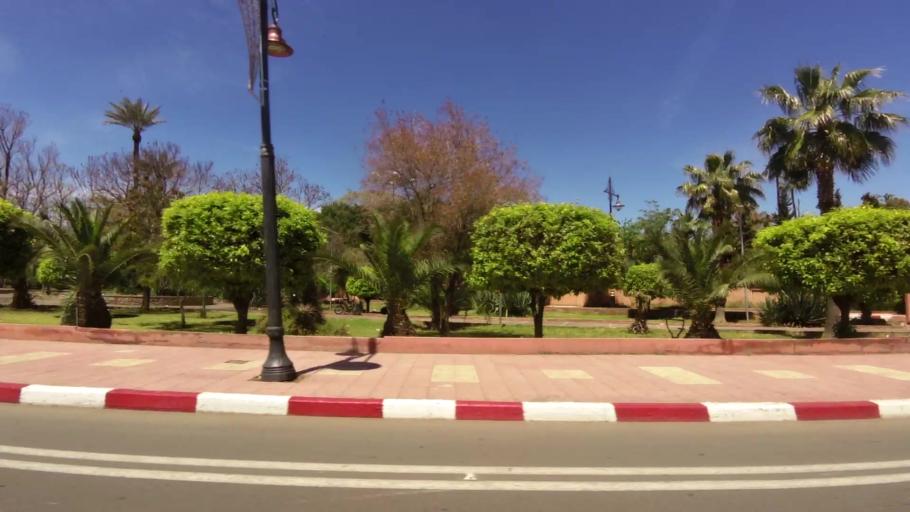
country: MA
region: Marrakech-Tensift-Al Haouz
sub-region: Marrakech
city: Marrakesh
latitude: 31.6192
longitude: -8.0050
